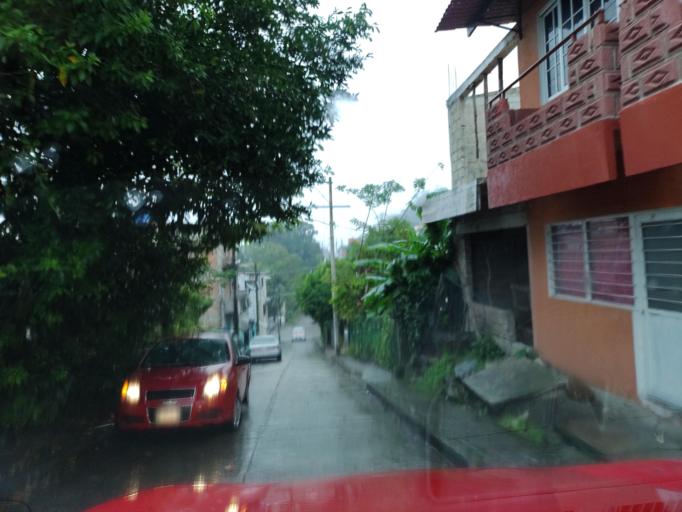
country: MX
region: Veracruz
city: Papantla de Olarte
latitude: 20.4409
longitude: -97.3355
